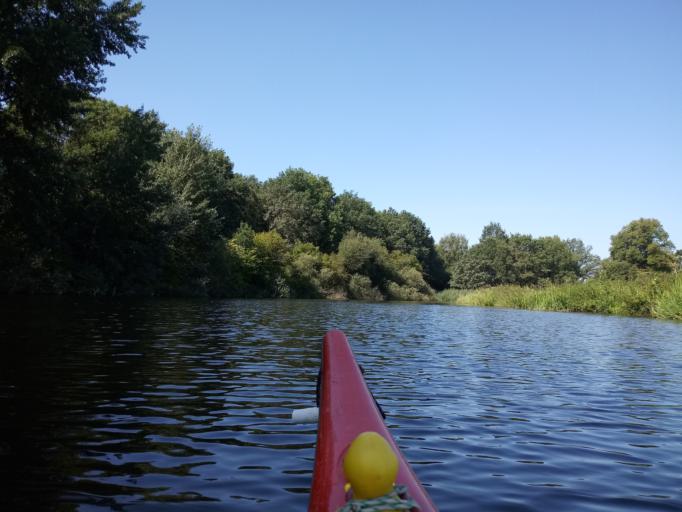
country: NL
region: Gelderland
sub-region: Berkelland
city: Eibergen
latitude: 52.1041
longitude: 6.6658
